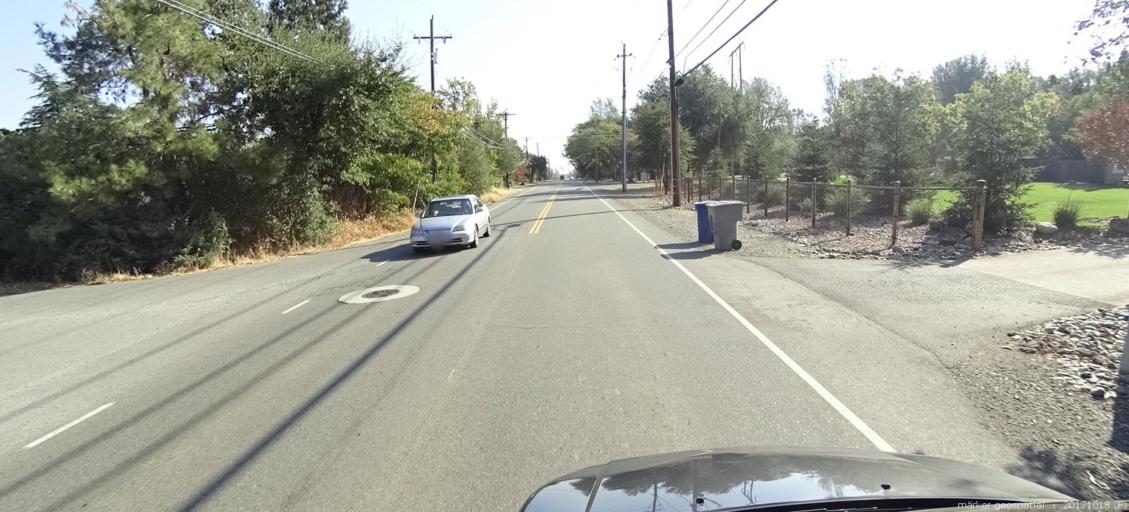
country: US
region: California
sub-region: Shasta County
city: Palo Cedro
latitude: 40.5347
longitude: -122.3071
